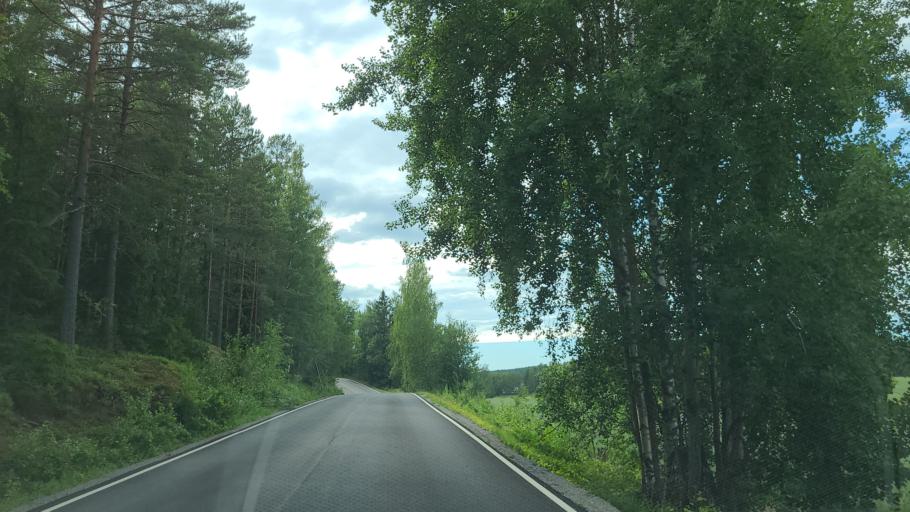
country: FI
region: Varsinais-Suomi
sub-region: Turku
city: Rymaettylae
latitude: 60.3256
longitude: 21.9620
